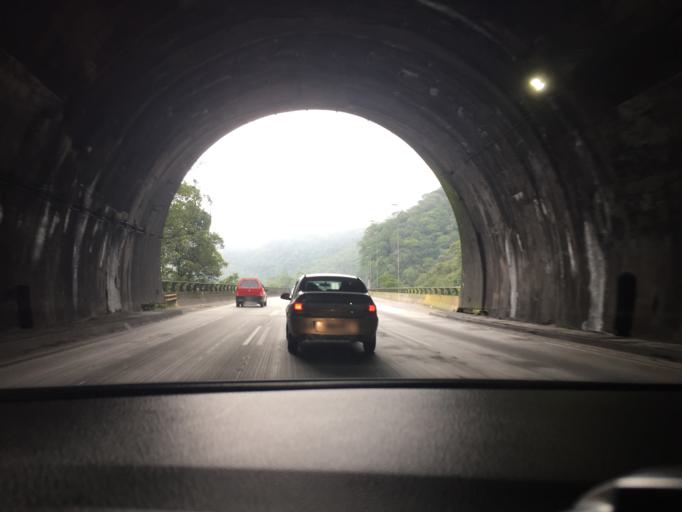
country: BR
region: Sao Paulo
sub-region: Cubatao
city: Cubatao
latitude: -23.9175
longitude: -46.5247
